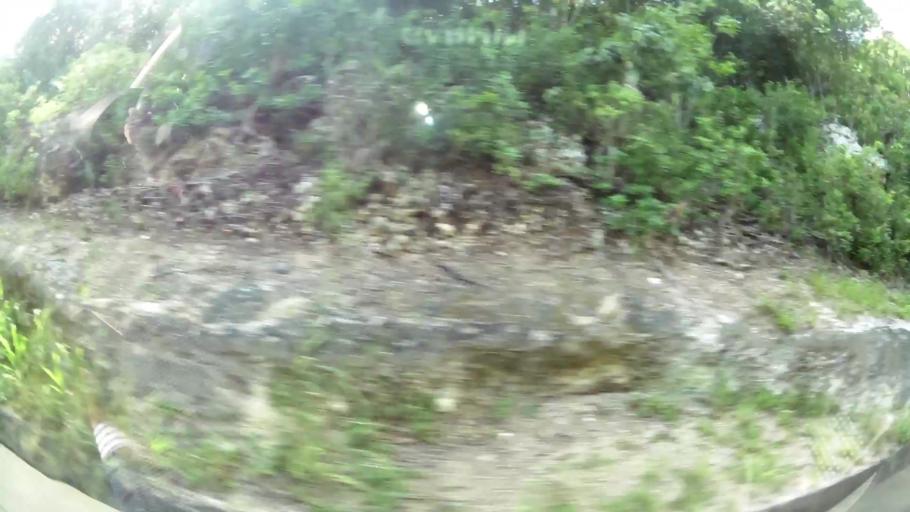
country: GP
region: Guadeloupe
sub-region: Guadeloupe
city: Anse-Bertrand
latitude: 16.4354
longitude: -61.4752
